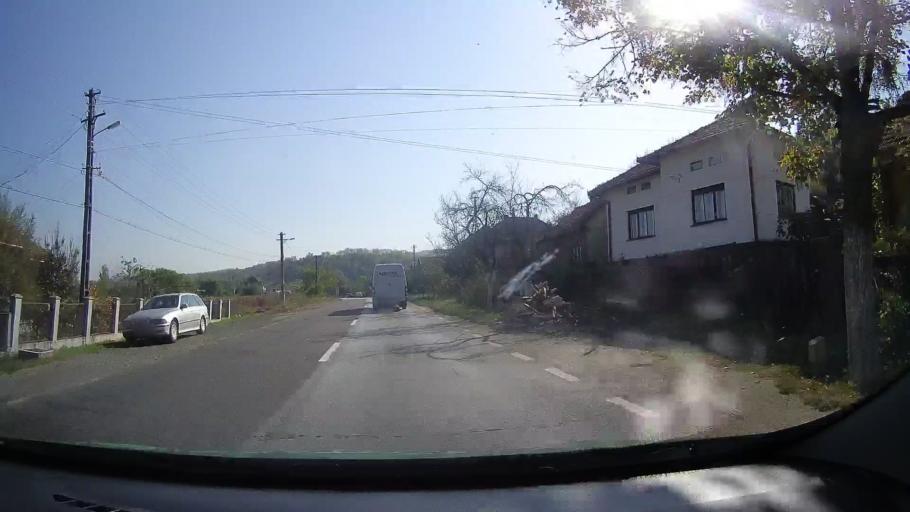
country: RO
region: Hunedoara
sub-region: Comuna Dobra
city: Dobra
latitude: 45.9084
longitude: 22.5785
